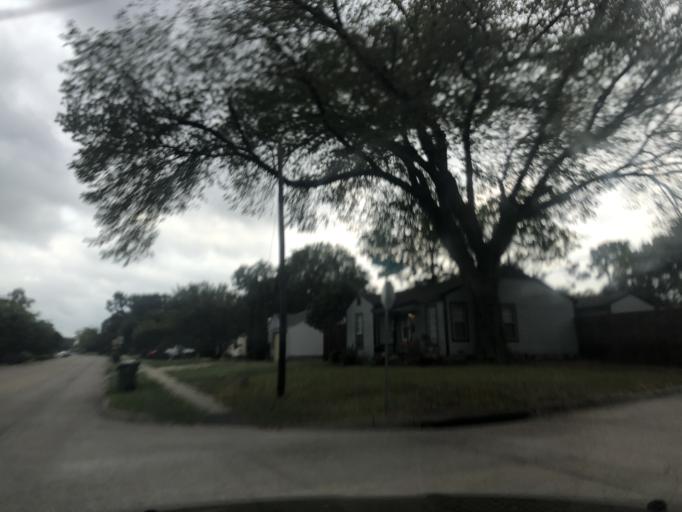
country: US
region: Texas
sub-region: Dallas County
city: Garland
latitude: 32.8872
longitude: -96.6482
